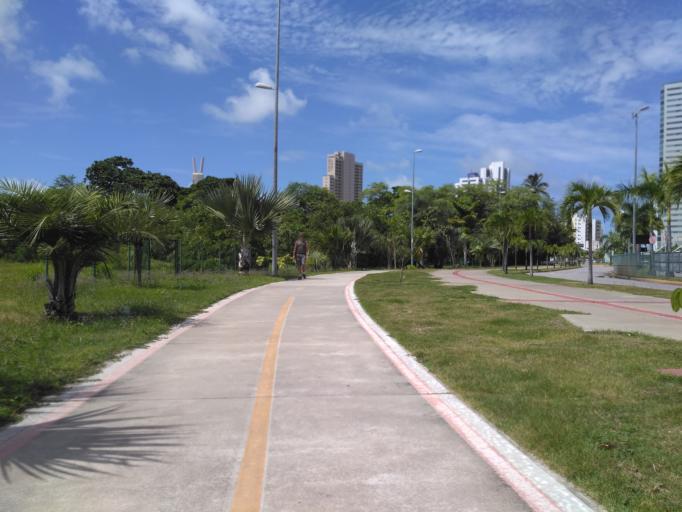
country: BR
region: Pernambuco
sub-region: Recife
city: Recife
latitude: -8.0845
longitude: -34.8945
